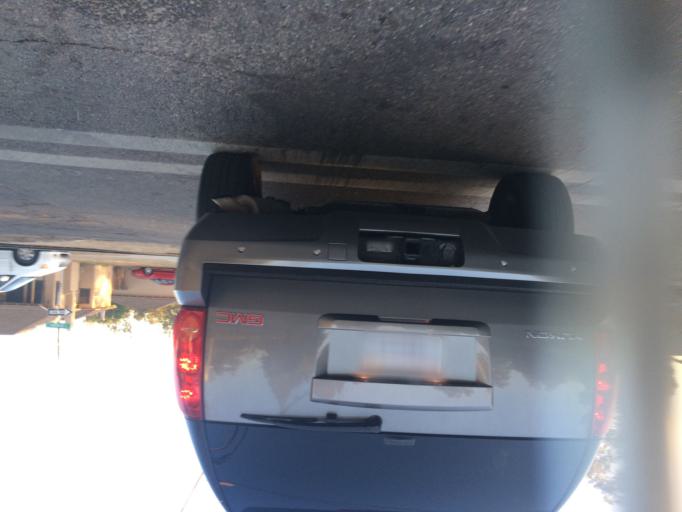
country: US
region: California
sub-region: Fresno County
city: Fresno
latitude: 36.7616
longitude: -119.7635
